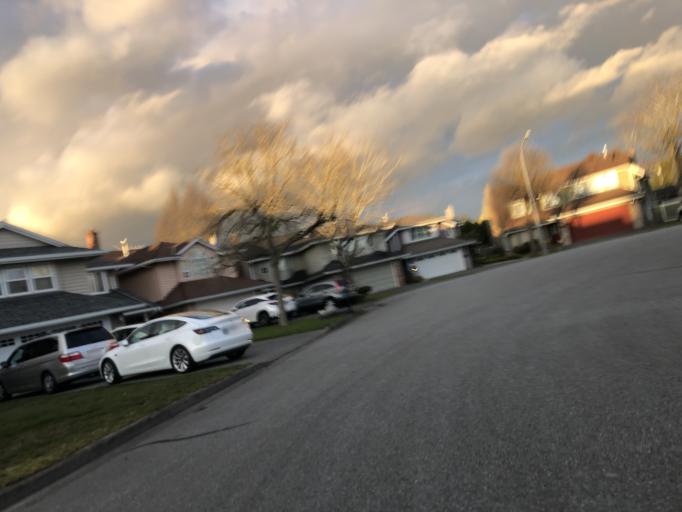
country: CA
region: British Columbia
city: Richmond
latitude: 49.1508
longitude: -123.1216
